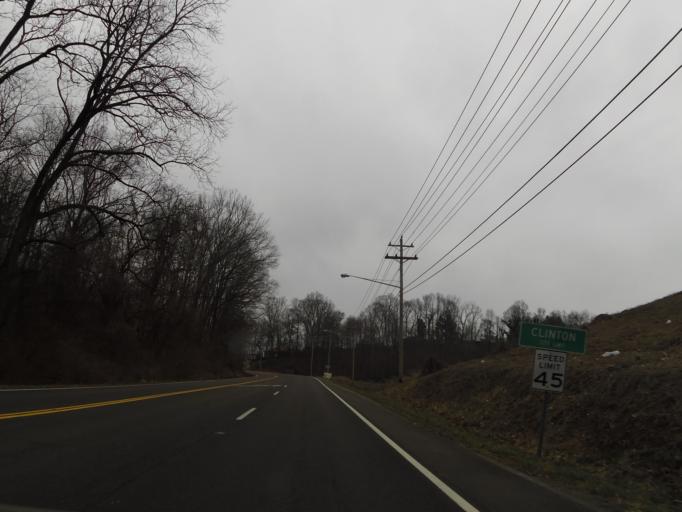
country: US
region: Tennessee
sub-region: Anderson County
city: Clinton
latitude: 36.1204
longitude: -84.1337
